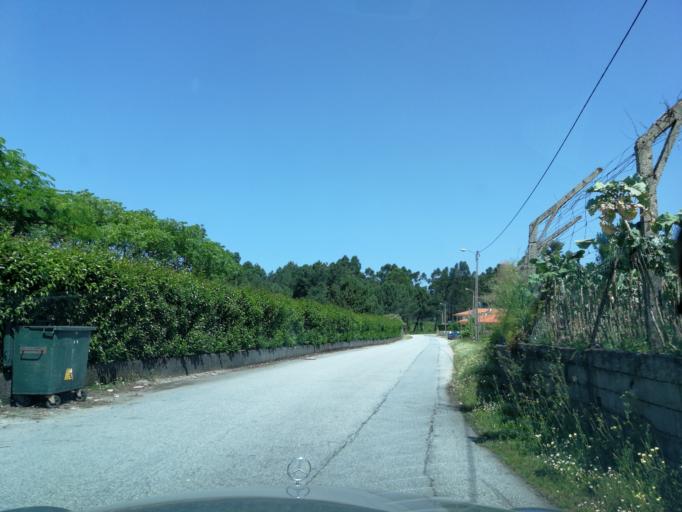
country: PT
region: Braga
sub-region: Braga
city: Adaufe
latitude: 41.5558
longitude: -8.3483
